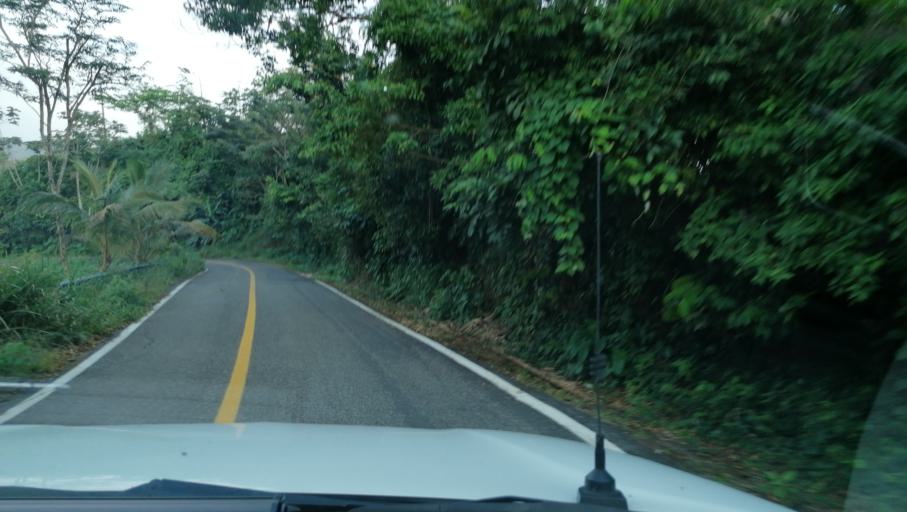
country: MX
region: Chiapas
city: Pichucalco
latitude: 17.5057
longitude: -93.2187
